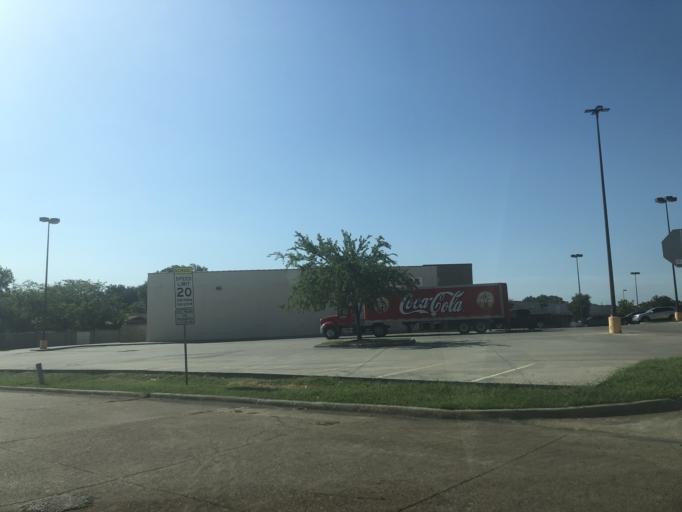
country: US
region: Texas
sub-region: Dallas County
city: Grand Prairie
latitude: 32.7574
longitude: -97.0181
